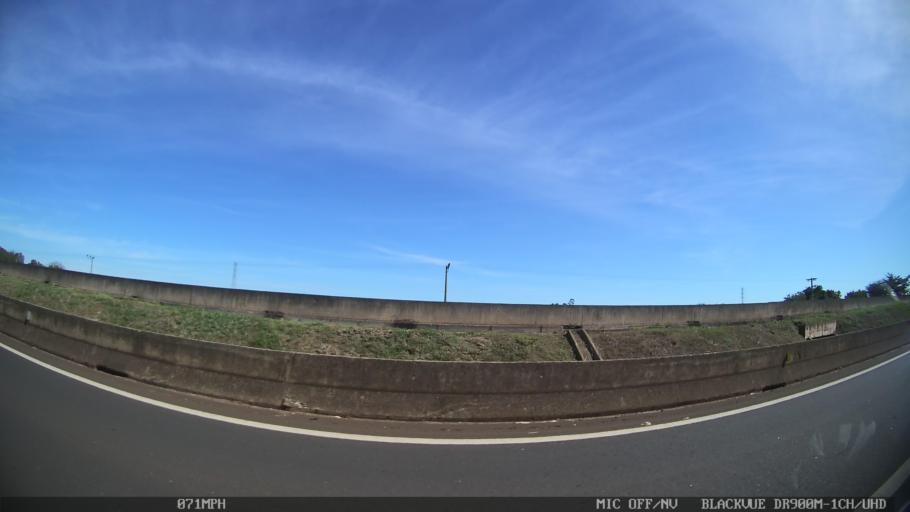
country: BR
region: Sao Paulo
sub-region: Porto Ferreira
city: Porto Ferreira
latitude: -21.8412
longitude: -47.4951
